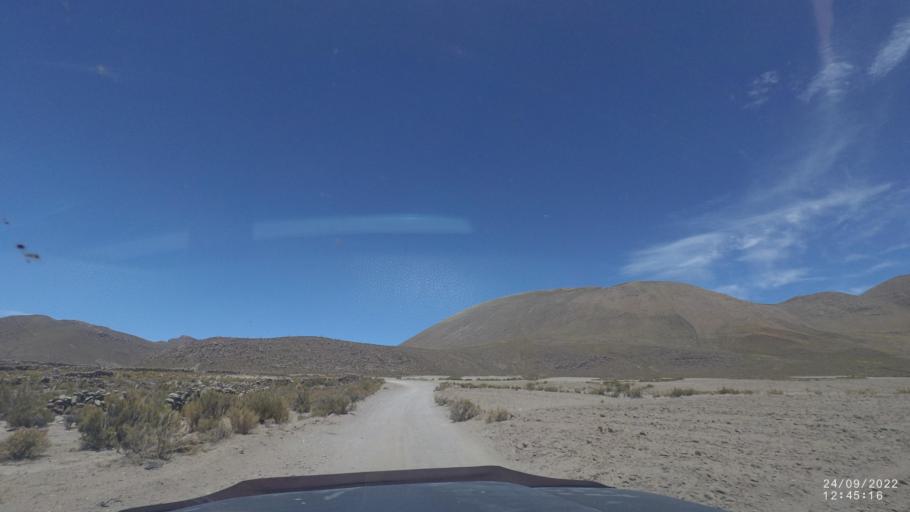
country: BO
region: Potosi
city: Colchani
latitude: -19.7980
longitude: -67.5777
